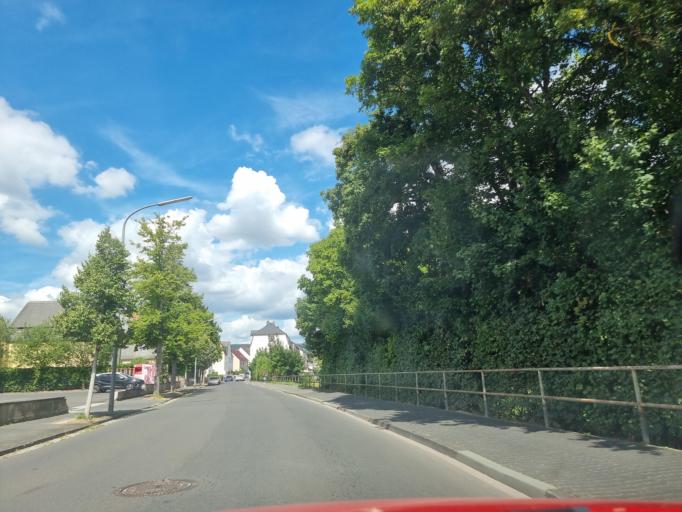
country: DE
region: Rheinland-Pfalz
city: Wittlich
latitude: 49.9820
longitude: 6.8893
